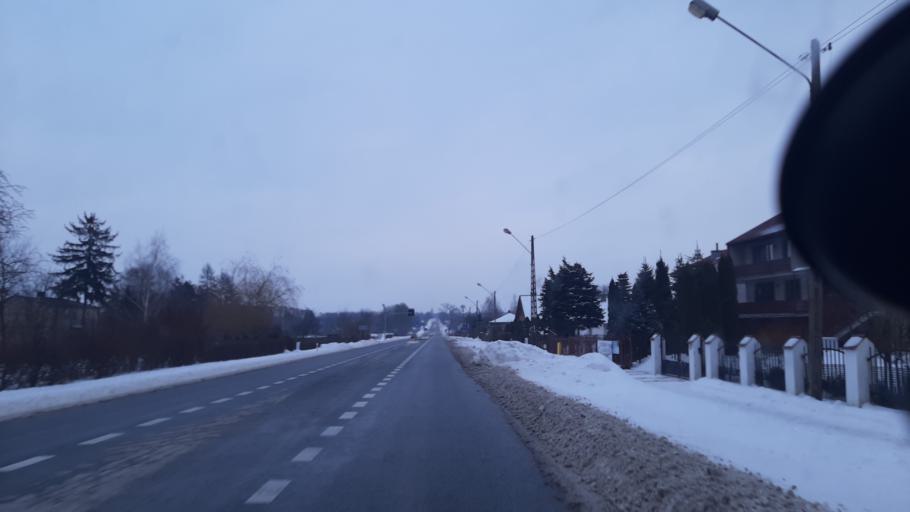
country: PL
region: Lublin Voivodeship
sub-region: Powiat lubelski
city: Garbow
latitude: 51.3634
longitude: 22.3011
